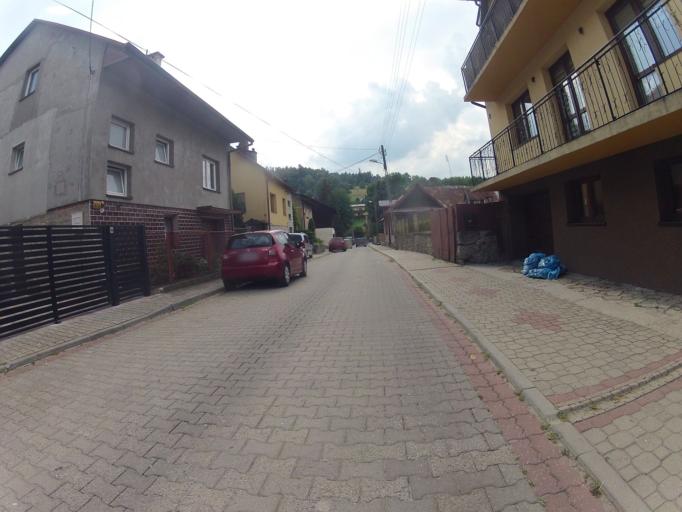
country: PL
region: Lesser Poland Voivodeship
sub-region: Powiat nowosadecki
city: Stary Sacz
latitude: 49.5630
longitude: 20.6331
